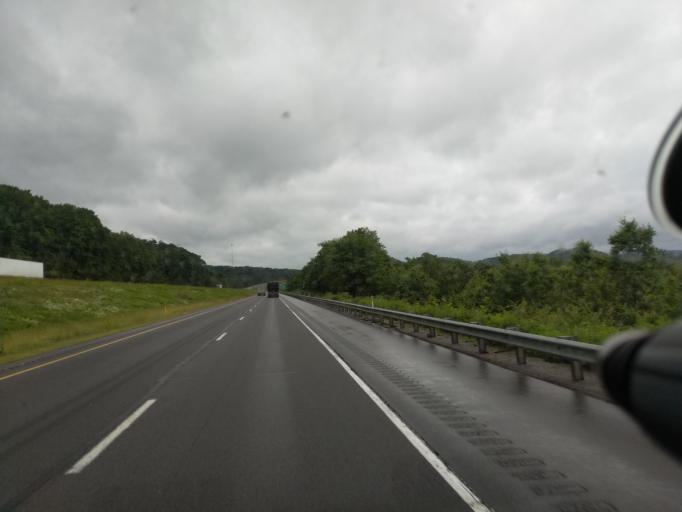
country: US
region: Pennsylvania
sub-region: Clearfield County
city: Treasure Lake
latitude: 41.1220
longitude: -78.6679
